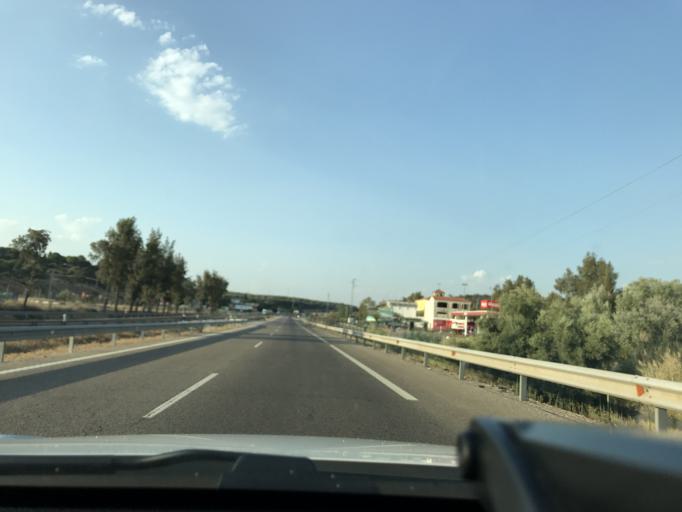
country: ES
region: Andalusia
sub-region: Provincia de Jaen
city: Espeluy
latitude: 38.0779
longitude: -3.8473
